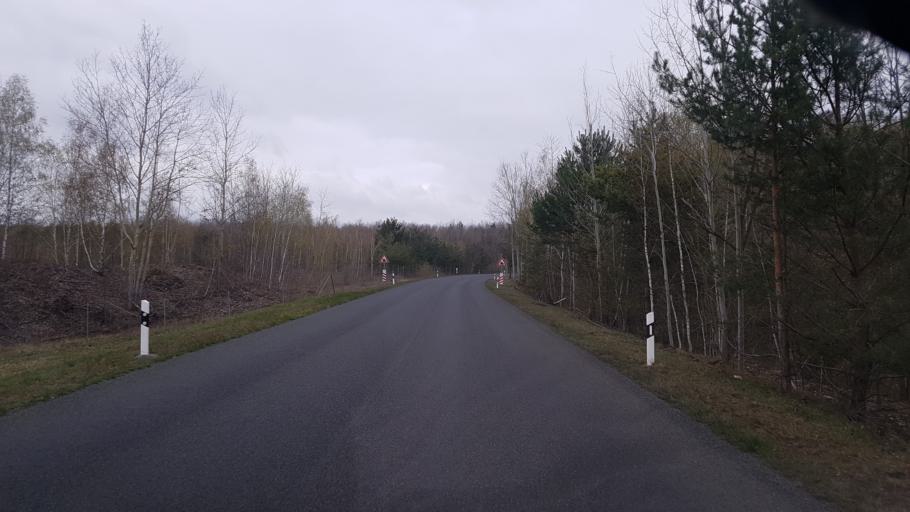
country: DE
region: Brandenburg
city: Lauchhammer
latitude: 51.4833
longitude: 13.7915
